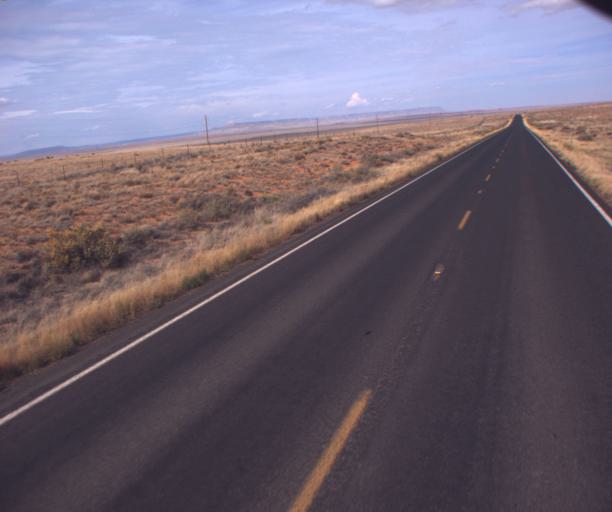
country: US
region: Arizona
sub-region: Apache County
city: Chinle
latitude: 35.9586
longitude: -109.5945
